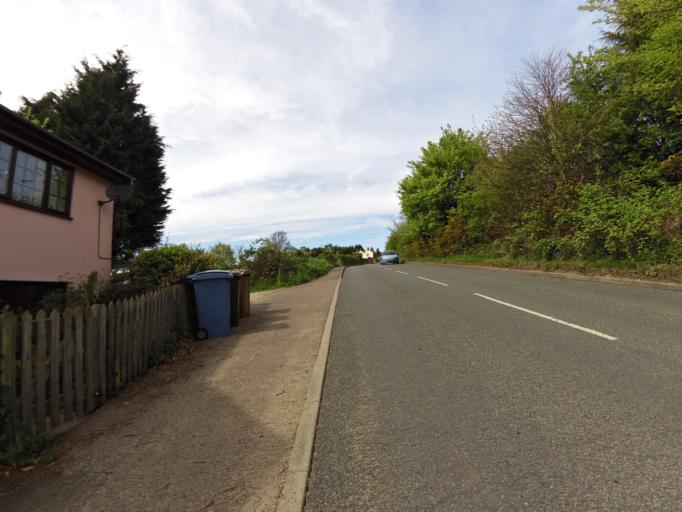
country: GB
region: England
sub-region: Suffolk
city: Ipswich
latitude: 51.9796
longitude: 1.1583
